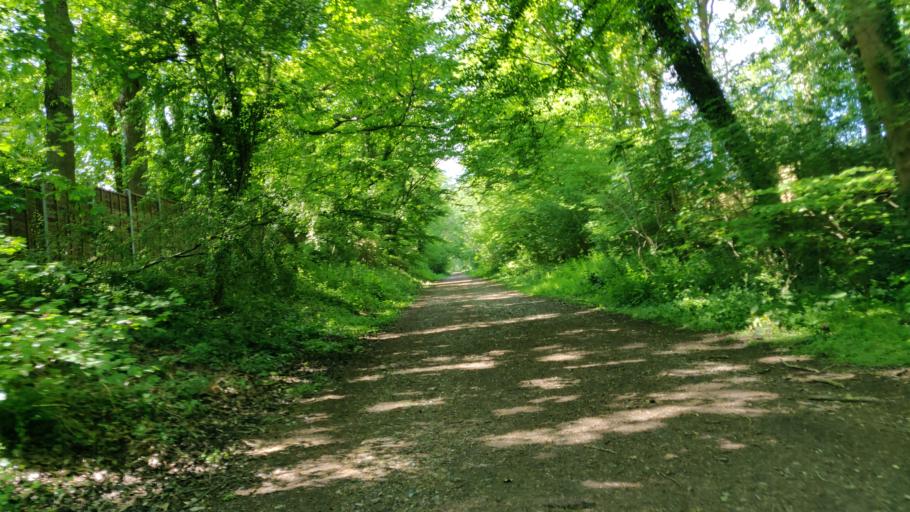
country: GB
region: England
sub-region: West Sussex
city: Rudgwick
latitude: 51.0874
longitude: -0.4477
